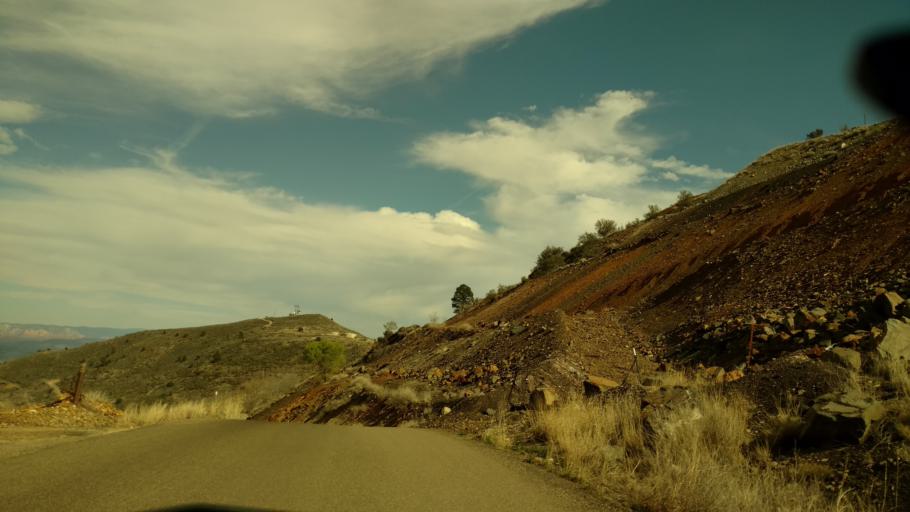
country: US
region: Arizona
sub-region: Yavapai County
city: Clarkdale
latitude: 34.7571
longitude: -112.1275
